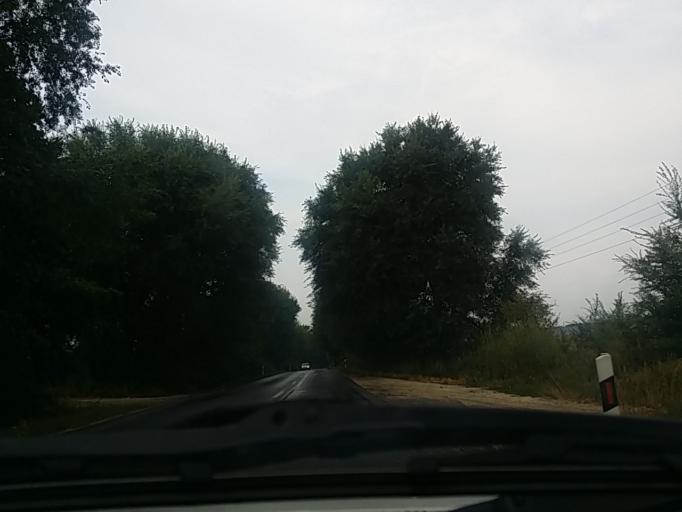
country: HU
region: Pest
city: Zsambek
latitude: 47.5414
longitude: 18.7455
